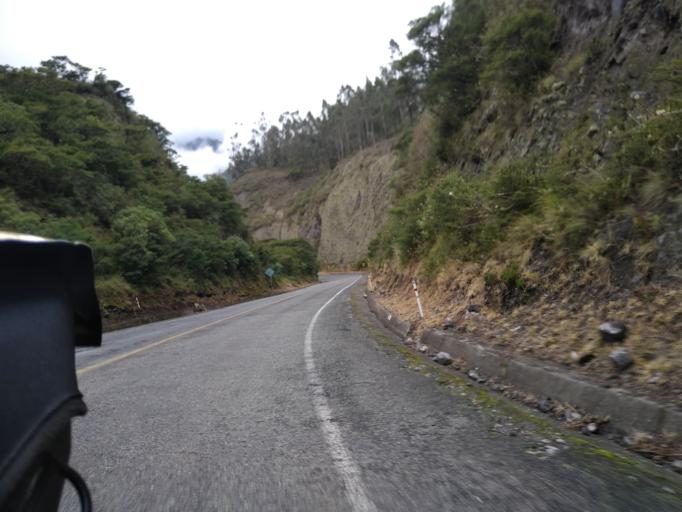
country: EC
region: Chimborazo
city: Guano
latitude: -1.5214
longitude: -78.5102
